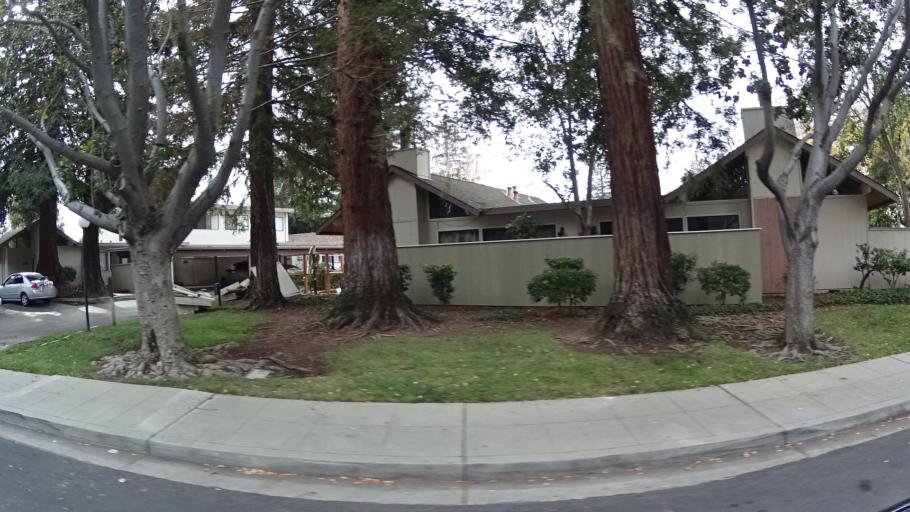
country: US
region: California
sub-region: Santa Clara County
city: Sunnyvale
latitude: 37.3687
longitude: -122.0427
